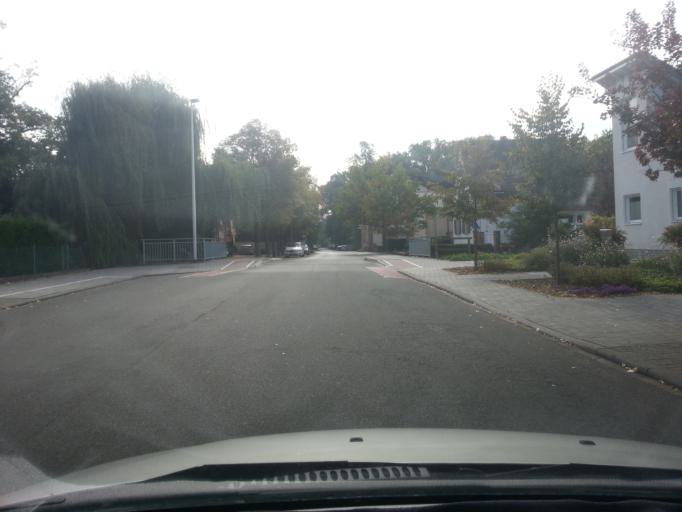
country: DE
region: Rheinland-Pfalz
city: Hassloch
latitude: 49.3478
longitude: 8.2619
